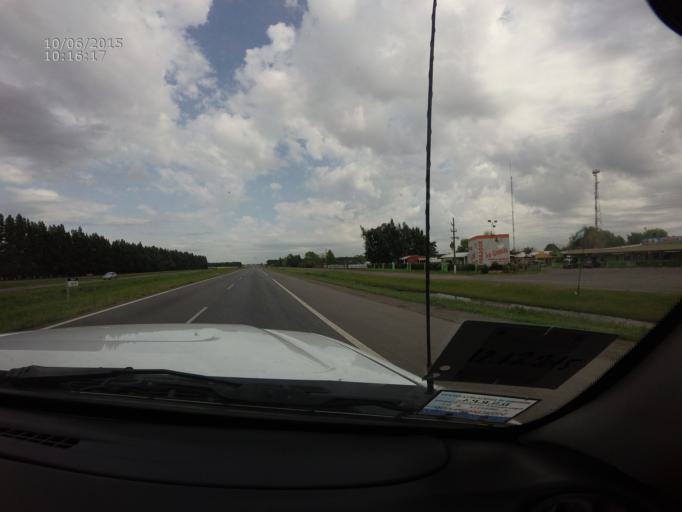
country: AR
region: Buenos Aires
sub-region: Partido de San Pedro
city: San Pedro
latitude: -33.7558
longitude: -59.7492
